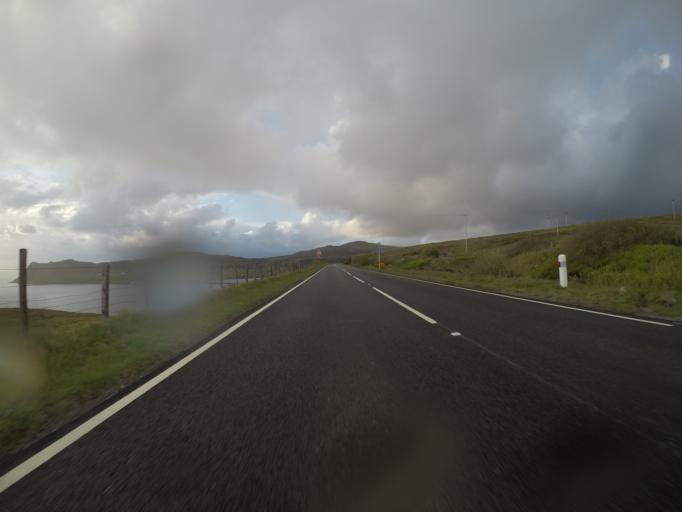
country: GB
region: Scotland
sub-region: Highland
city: Portree
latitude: 57.5753
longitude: -6.3654
